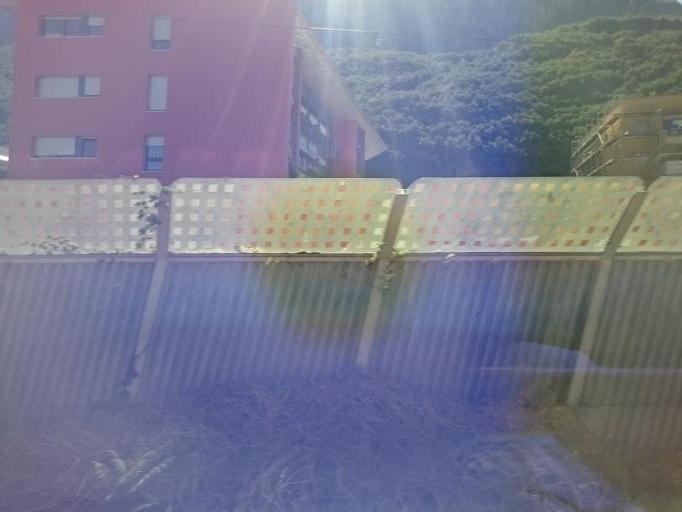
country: IT
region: Trentino-Alto Adige
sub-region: Bolzano
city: San Giacomo
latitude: 46.4708
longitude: 11.3351
